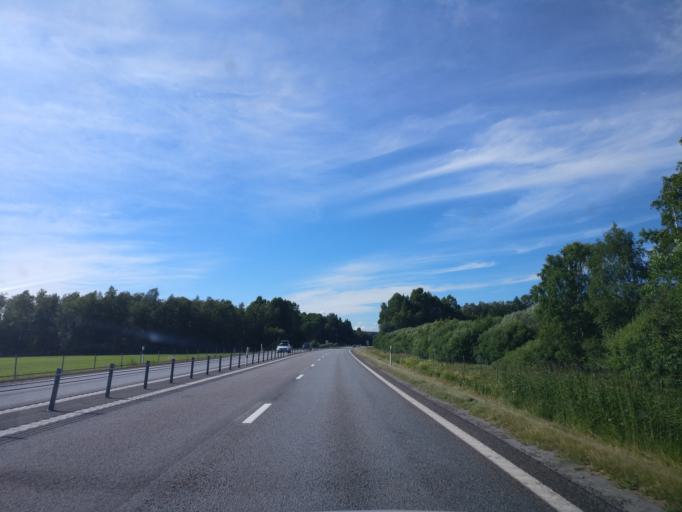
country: SE
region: Vaermland
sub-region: Kils Kommun
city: Kil
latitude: 59.4392
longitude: 13.3895
